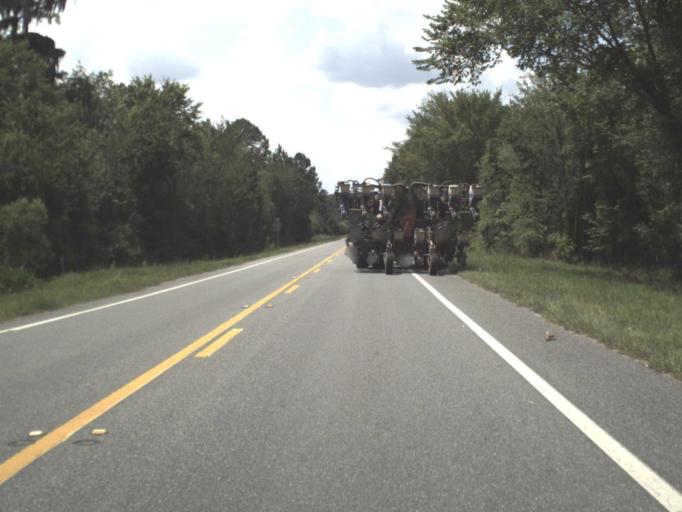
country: US
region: Florida
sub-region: Hamilton County
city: Jasper
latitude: 30.5523
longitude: -83.0621
